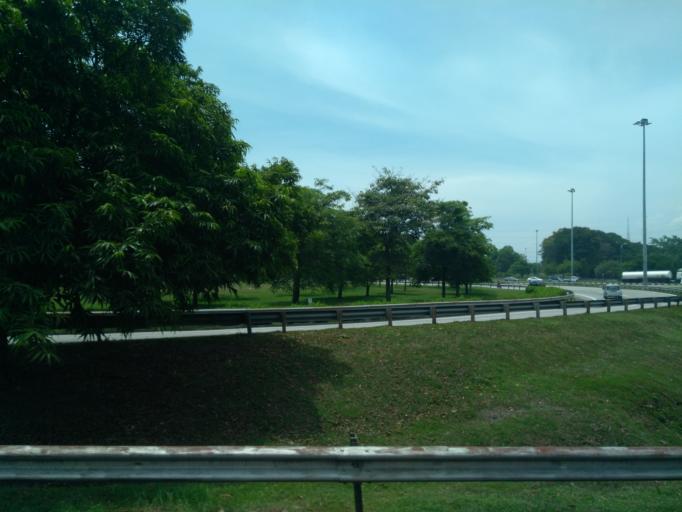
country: MY
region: Penang
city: Perai
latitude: 5.3745
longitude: 100.4040
